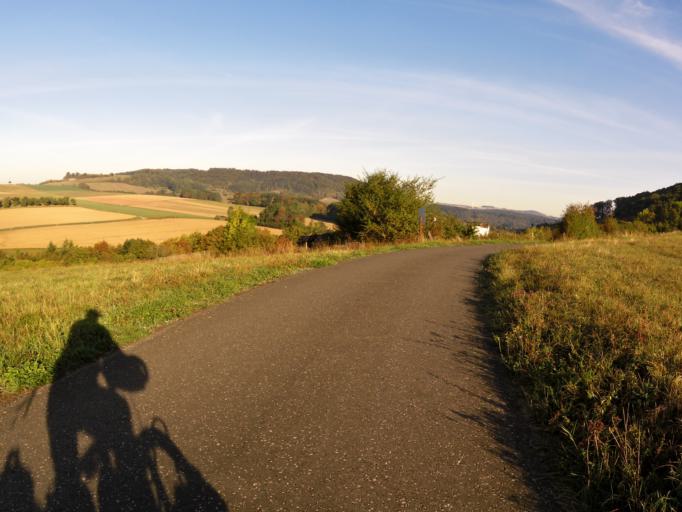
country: DE
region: Rheinland-Pfalz
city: Holsthum
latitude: 49.8973
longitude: 6.4162
